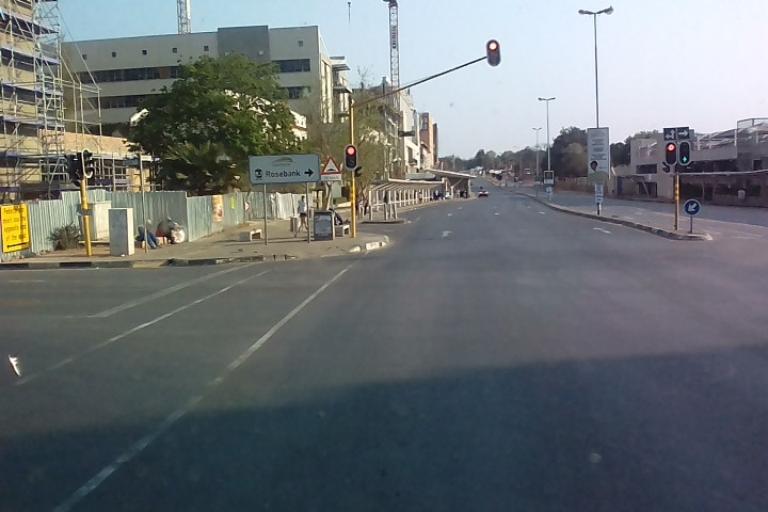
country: ZA
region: Gauteng
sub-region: City of Johannesburg Metropolitan Municipality
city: Johannesburg
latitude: -26.1476
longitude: 28.0445
